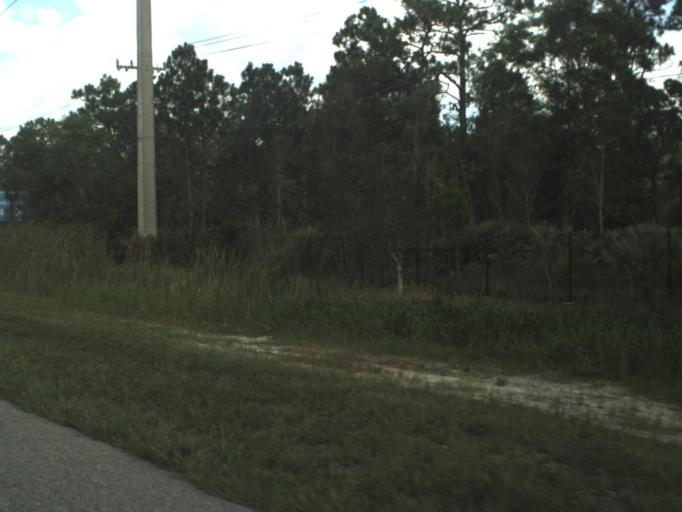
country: US
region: Florida
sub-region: Palm Beach County
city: Limestone Creek
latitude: 26.8920
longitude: -80.2750
